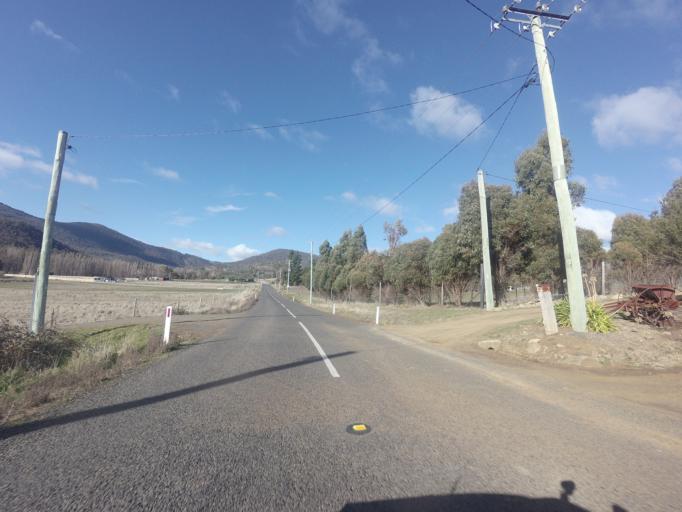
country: AU
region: Tasmania
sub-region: Derwent Valley
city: New Norfolk
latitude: -42.7972
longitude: 147.1319
